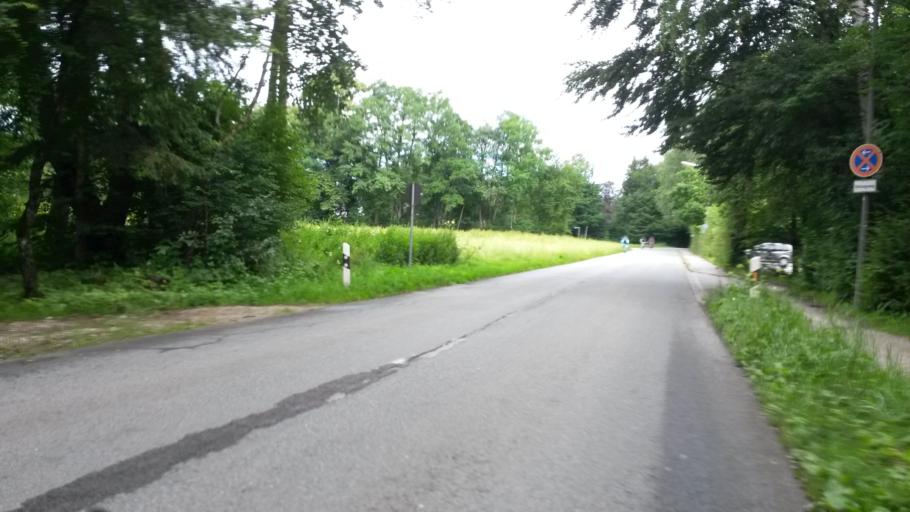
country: DE
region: Bavaria
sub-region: Upper Bavaria
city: Prien am Chiemsee
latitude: 47.8427
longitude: 12.3706
